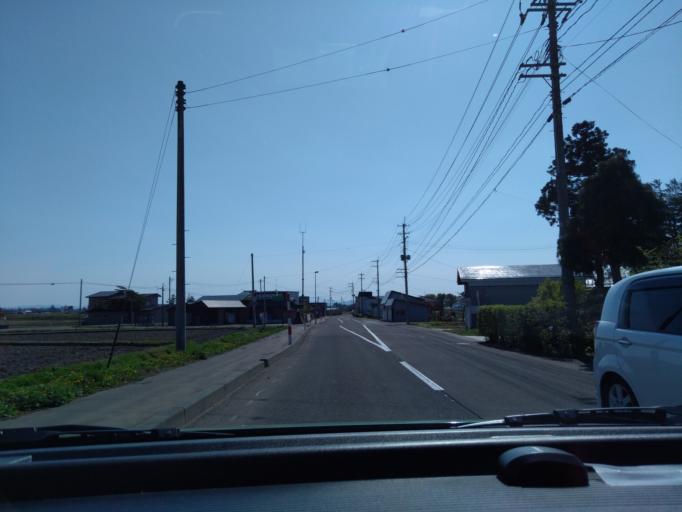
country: JP
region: Akita
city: Omagari
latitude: 39.4507
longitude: 140.5735
